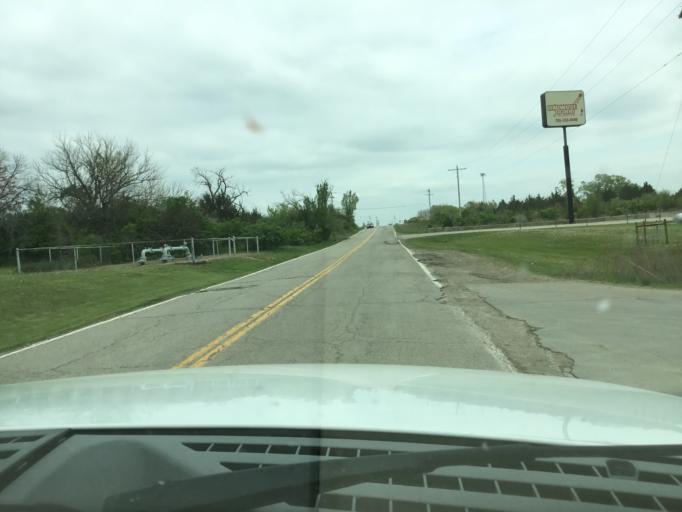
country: US
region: Kansas
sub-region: Shawnee County
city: Topeka
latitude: 39.0297
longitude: -95.6284
